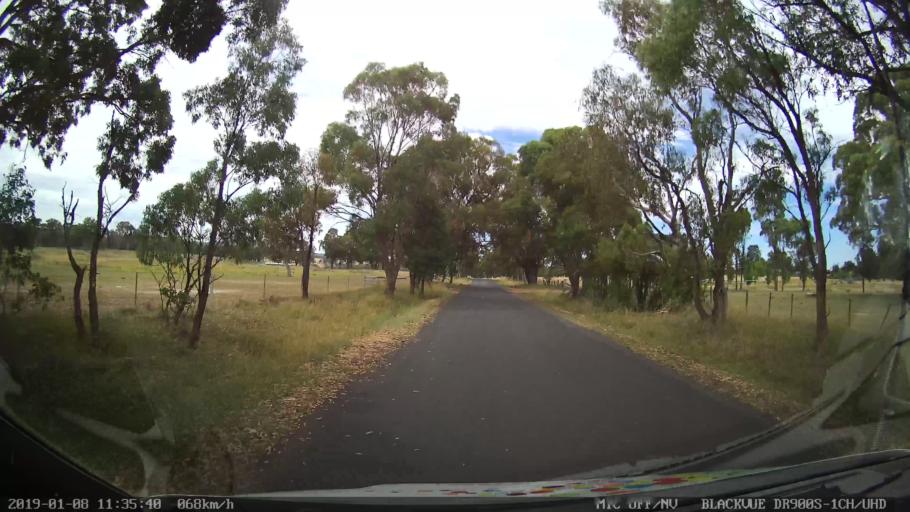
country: AU
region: New South Wales
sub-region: Guyra
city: Guyra
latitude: -30.3395
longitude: 151.5385
